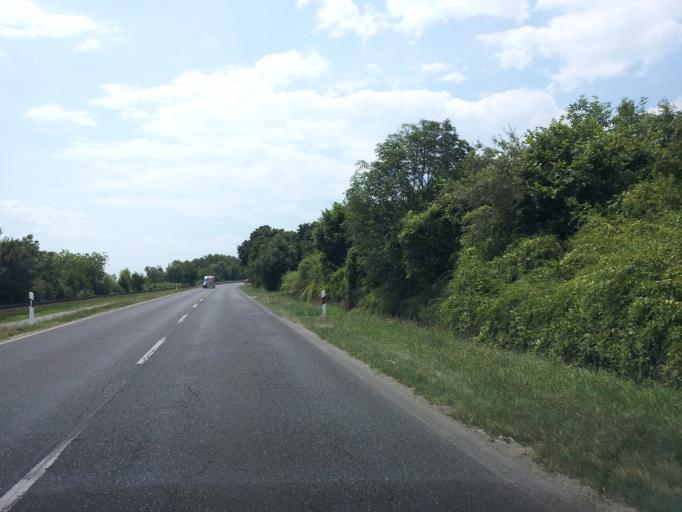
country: HU
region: Veszprem
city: Balatonalmadi
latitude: 47.0025
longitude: 18.0008
